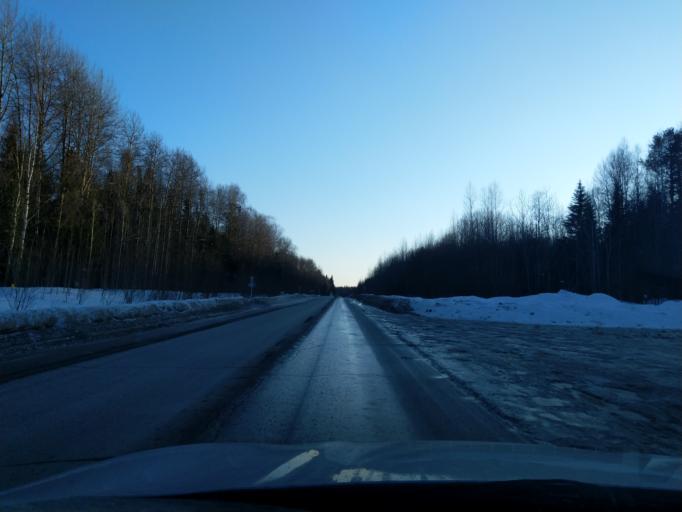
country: RU
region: Perm
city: Dobryanka
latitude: 58.4519
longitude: 56.5462
